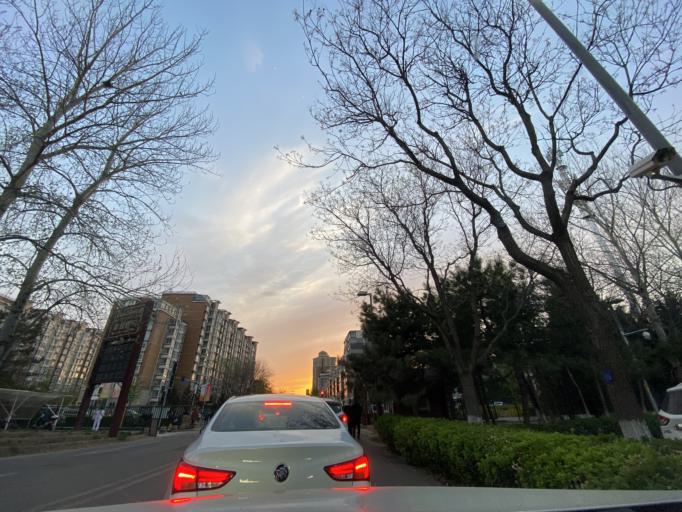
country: CN
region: Beijing
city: Qinghe
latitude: 40.0123
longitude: 116.3692
